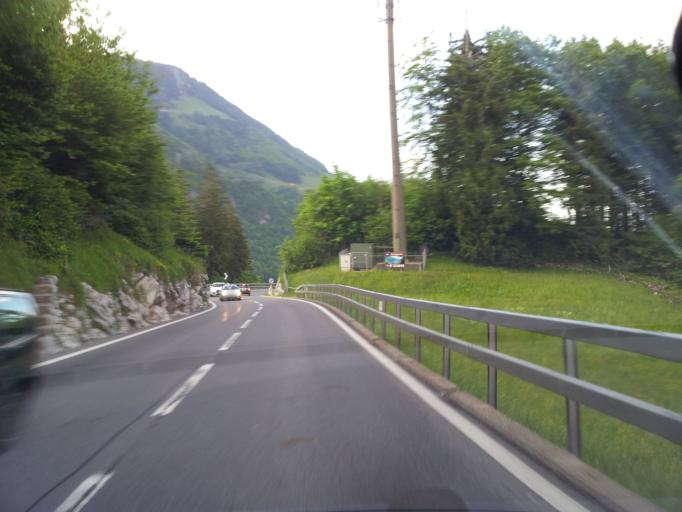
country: CH
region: Obwalden
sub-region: Obwalden
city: Lungern
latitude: 46.7745
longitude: 8.1419
